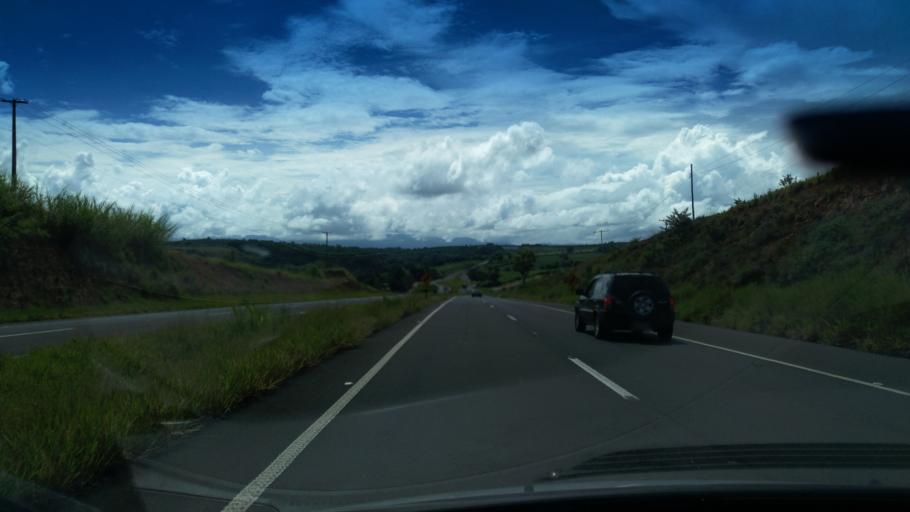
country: BR
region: Sao Paulo
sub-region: Santo Antonio Do Jardim
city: Espirito Santo do Pinhal
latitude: -22.1694
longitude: -46.7418
